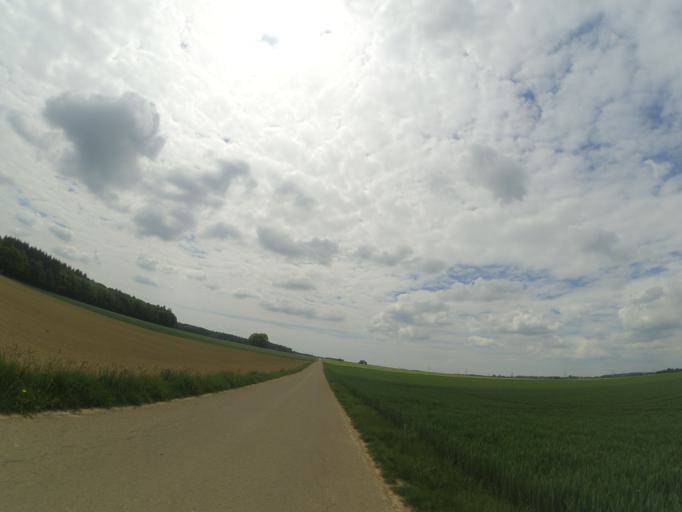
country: DE
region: Baden-Wuerttemberg
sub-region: Tuebingen Region
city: Blaubeuren
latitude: 48.4332
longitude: 9.8291
